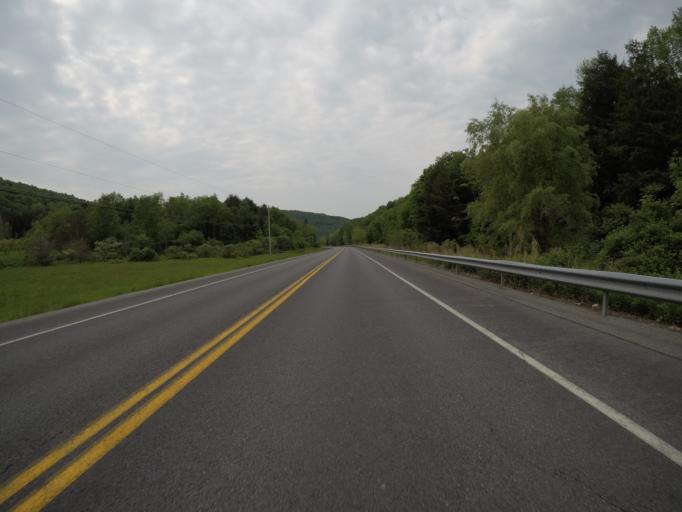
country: US
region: New York
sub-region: Sullivan County
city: Livingston Manor
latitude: 41.9767
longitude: -74.8946
